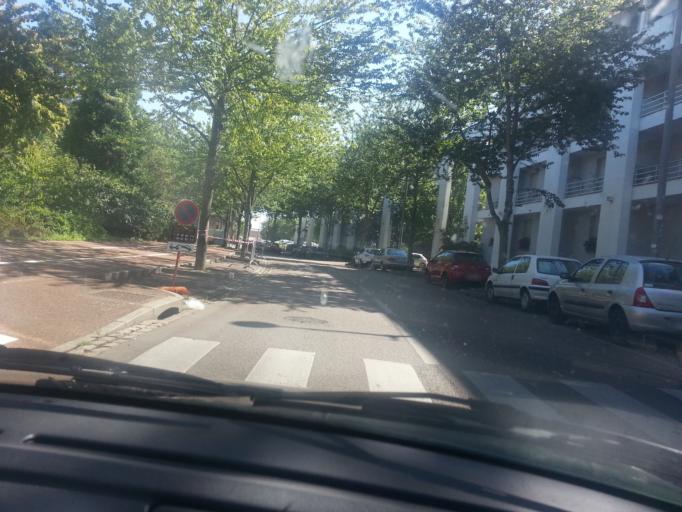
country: FR
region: Bourgogne
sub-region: Departement de Saone-et-Loire
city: Chalon-sur-Saone
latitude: 46.7787
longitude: 4.8458
